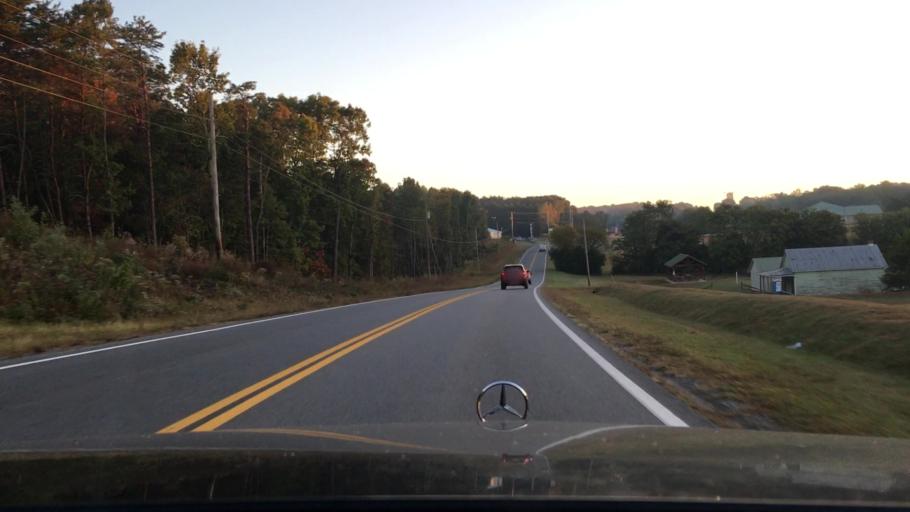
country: US
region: Virginia
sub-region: Campbell County
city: Timberlake
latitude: 37.3174
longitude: -79.2377
